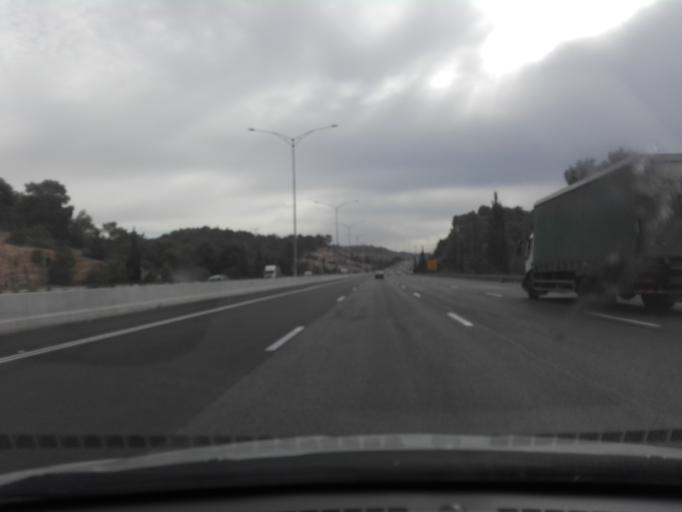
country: IL
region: Central District
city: Nehalim
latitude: 32.0308
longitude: 34.9576
